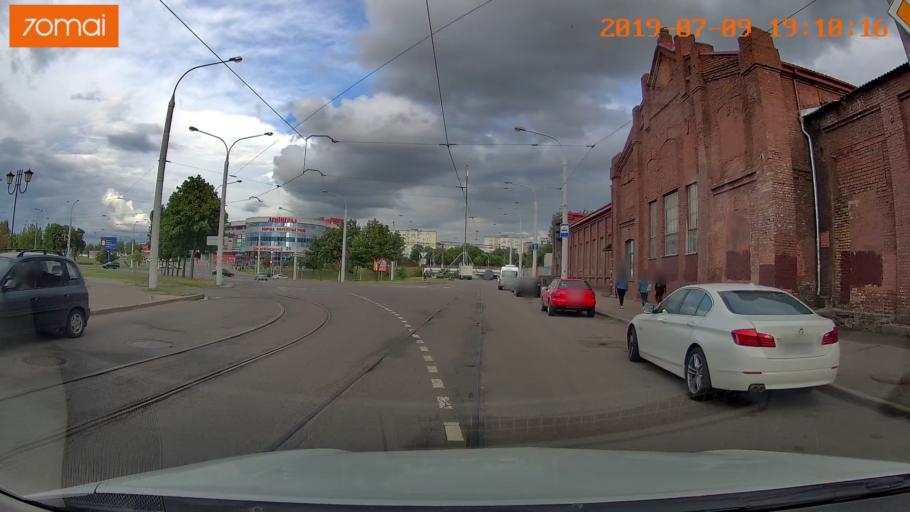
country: BY
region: Minsk
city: Minsk
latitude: 53.8891
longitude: 27.5772
